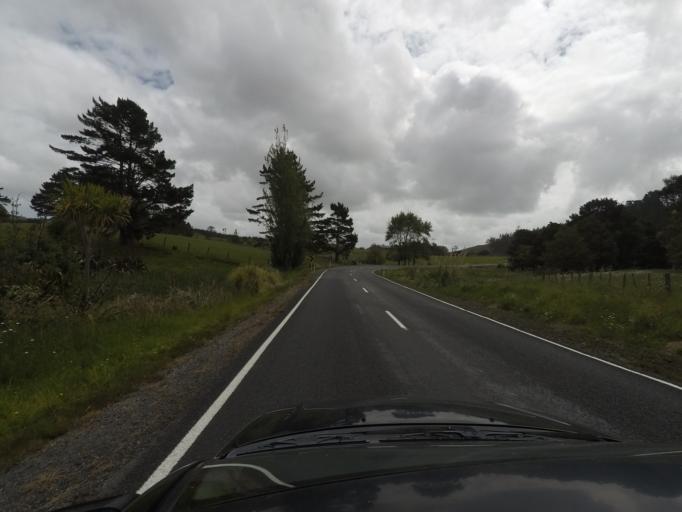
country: NZ
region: Auckland
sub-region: Auckland
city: Parakai
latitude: -36.5017
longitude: 174.4782
